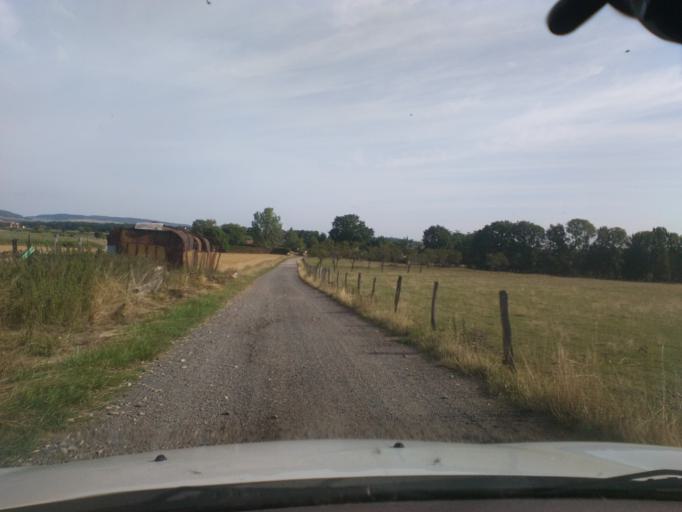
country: FR
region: Lorraine
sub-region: Departement des Vosges
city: Mirecourt
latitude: 48.3293
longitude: 6.0951
